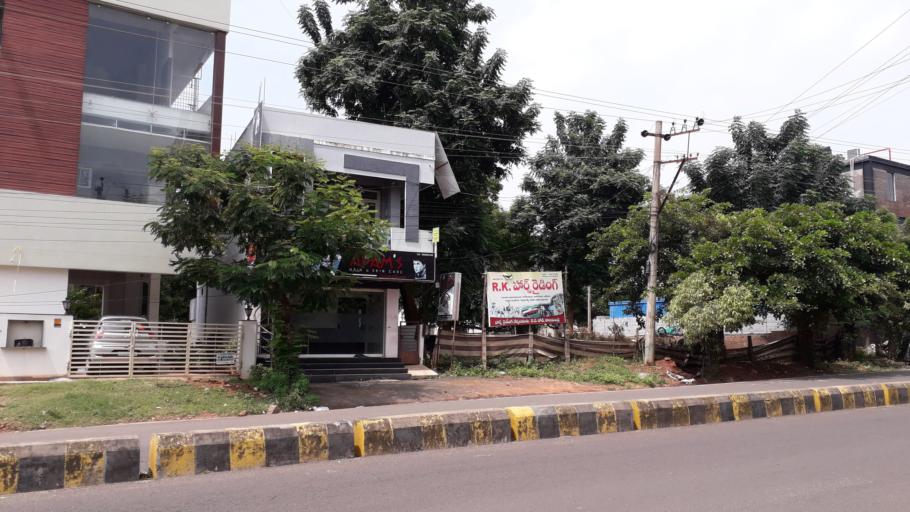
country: IN
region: Andhra Pradesh
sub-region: East Godavari
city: Rajahmundry
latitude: 17.0069
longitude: 81.8009
